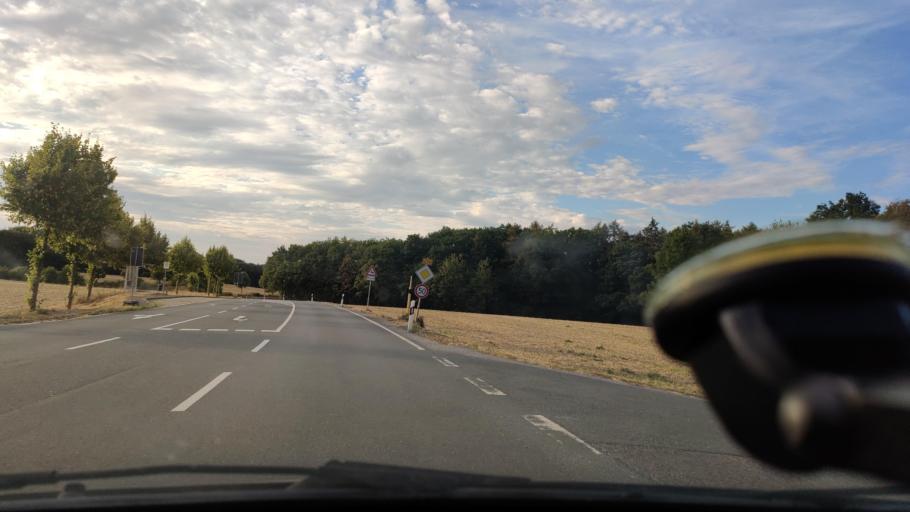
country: DE
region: North Rhine-Westphalia
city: Schwerte
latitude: 51.3982
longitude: 7.5827
